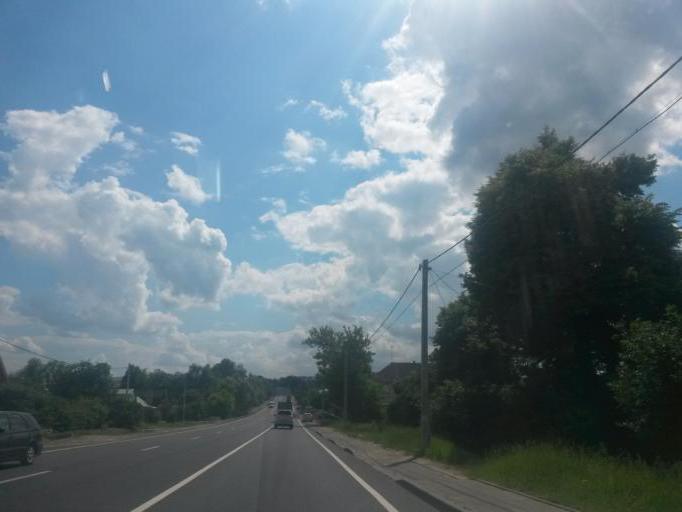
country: RU
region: Moskovskaya
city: Vostryakovo
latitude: 55.3850
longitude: 37.7859
